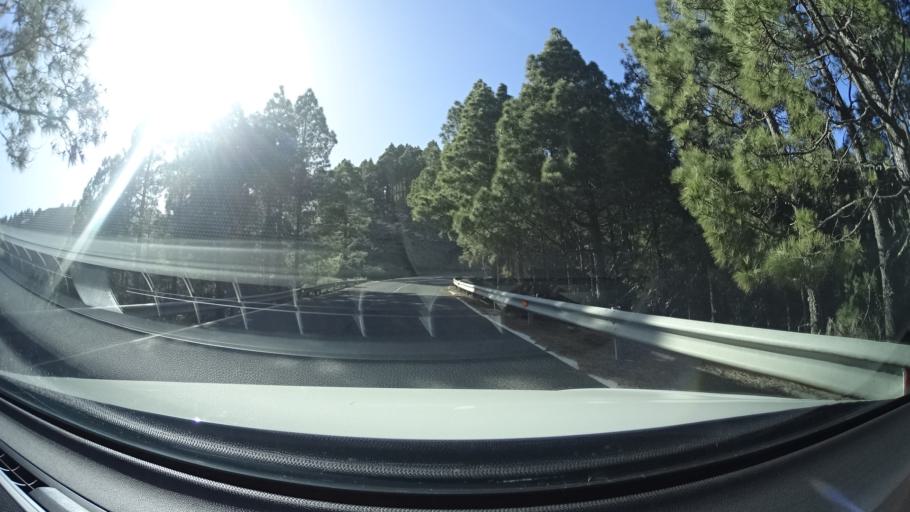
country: ES
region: Canary Islands
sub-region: Provincia de Las Palmas
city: Valsequillo de Gran Canaria
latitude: 27.9610
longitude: -15.5364
